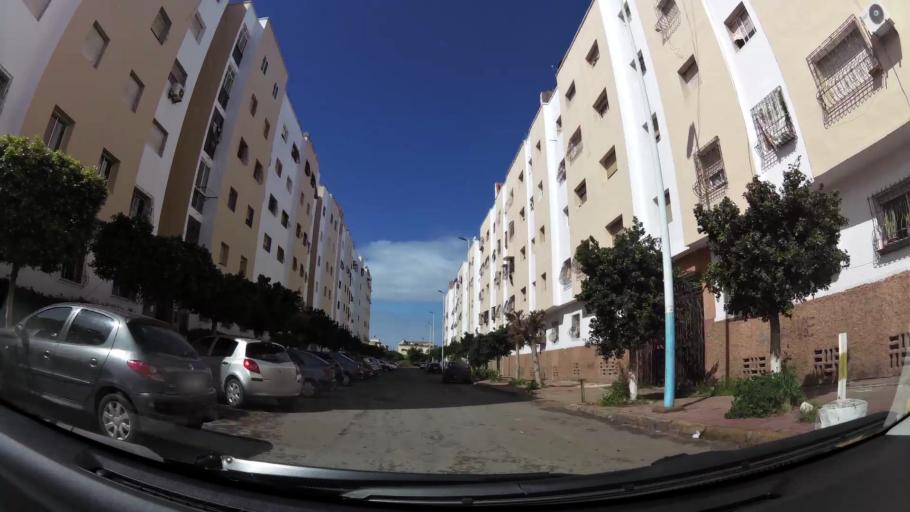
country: MA
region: Grand Casablanca
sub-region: Casablanca
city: Casablanca
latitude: 33.5655
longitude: -7.6782
